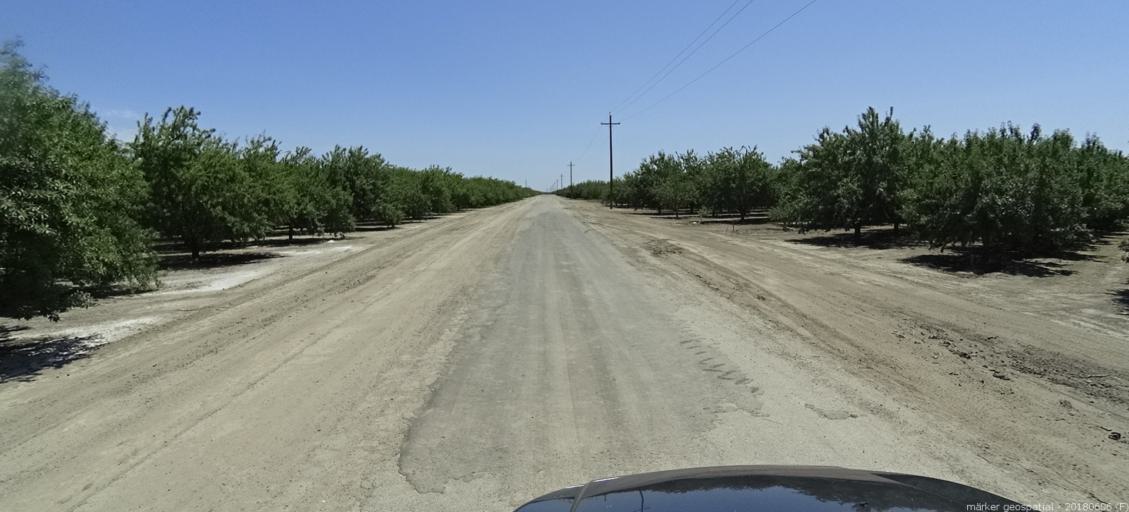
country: US
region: California
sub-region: Fresno County
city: Mendota
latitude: 36.7981
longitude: -120.3314
